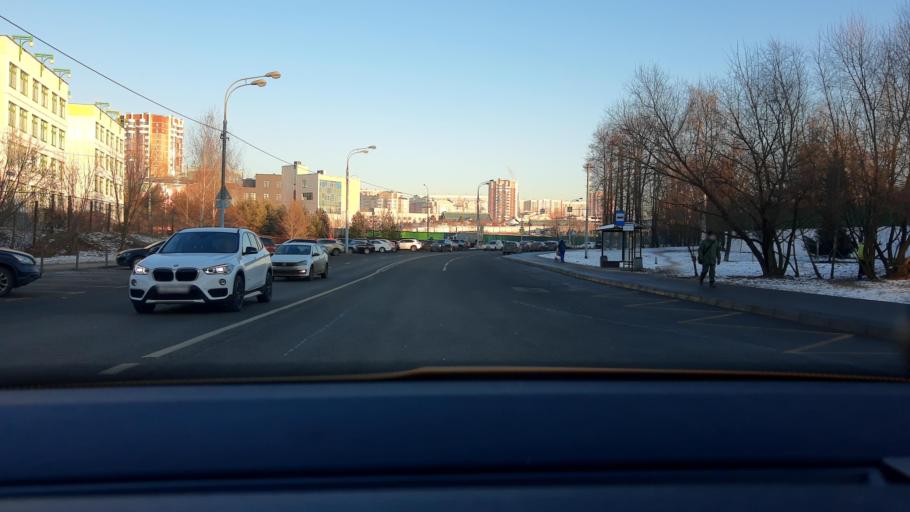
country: RU
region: Moscow
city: Khimki
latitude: 55.8994
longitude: 37.3812
